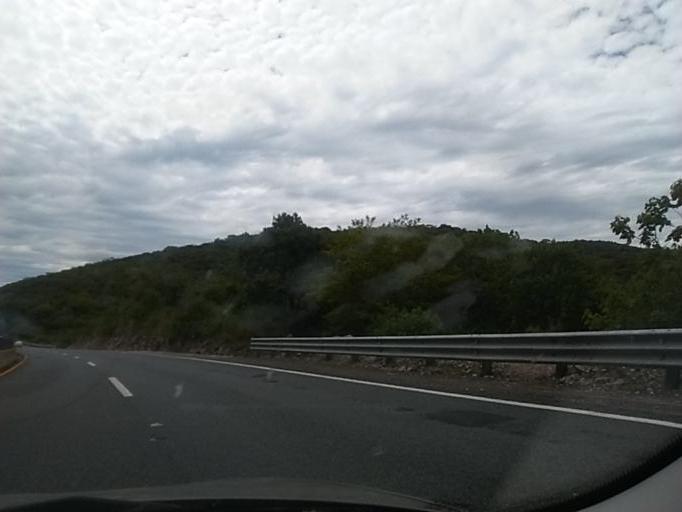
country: MX
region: Guerrero
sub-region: Huitzuco de los Figueroa
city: Ciudad de Huitzuco
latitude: 18.2551
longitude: -99.2151
